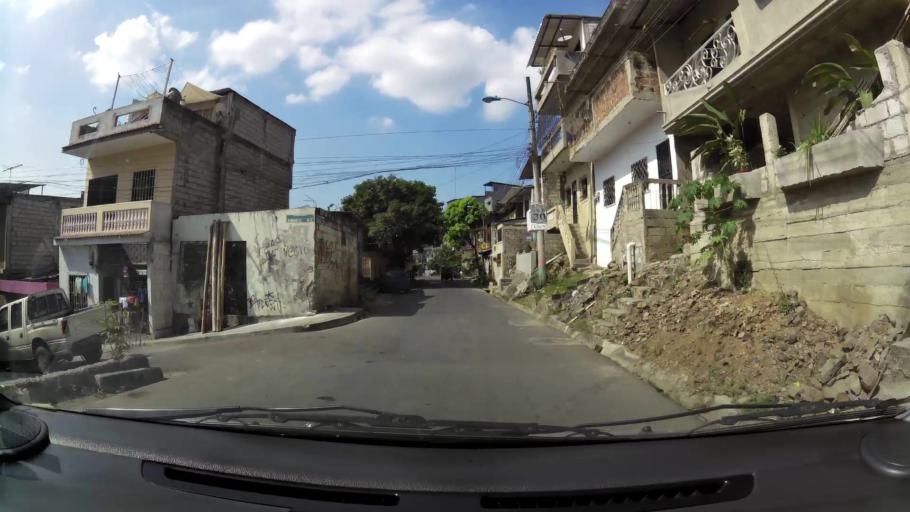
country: EC
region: Guayas
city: Guayaquil
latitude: -2.1506
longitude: -79.9381
